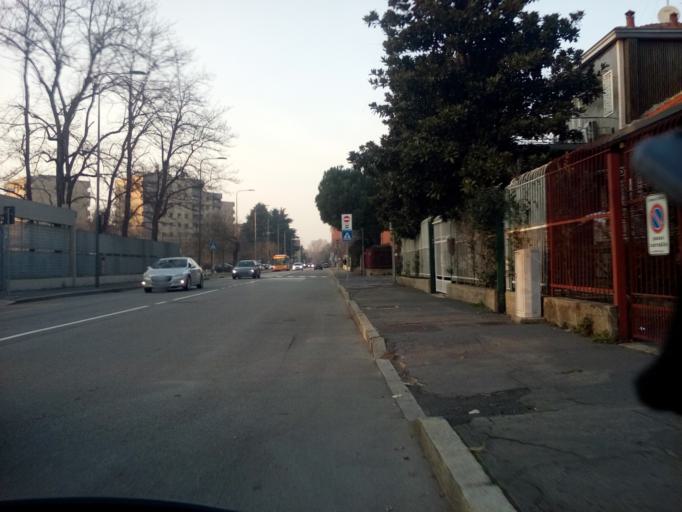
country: IT
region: Lombardy
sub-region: Citta metropolitana di Milano
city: Cesano Boscone
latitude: 45.4586
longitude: 9.0852
